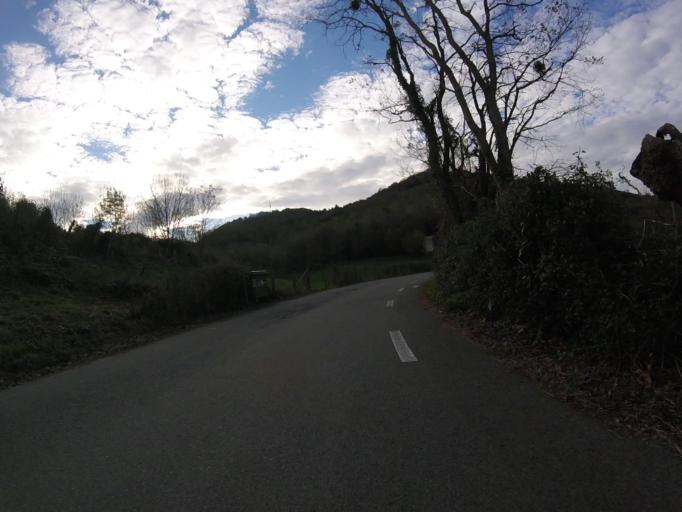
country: ES
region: Basque Country
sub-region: Provincia de Guipuzcoa
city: Errenteria
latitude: 43.3046
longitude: -1.9192
